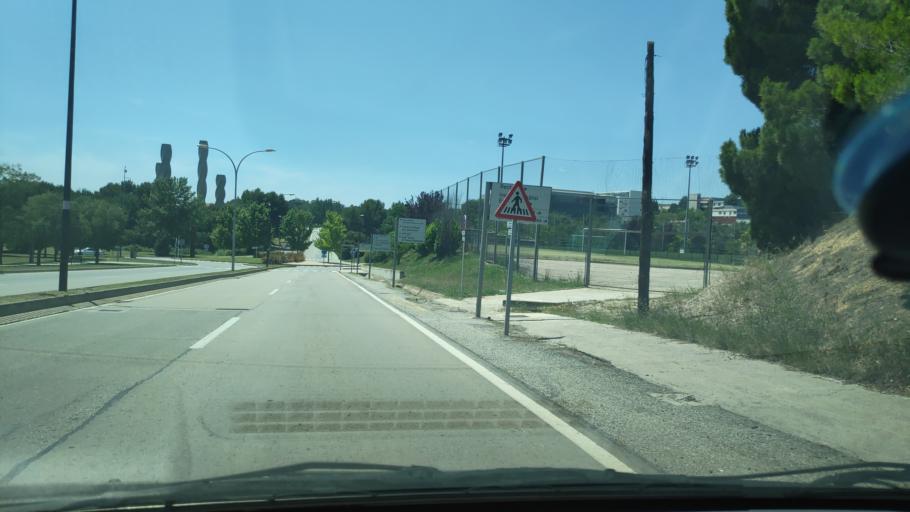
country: ES
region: Catalonia
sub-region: Provincia de Barcelona
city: Barbera del Valles
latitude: 41.4987
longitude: 2.1130
